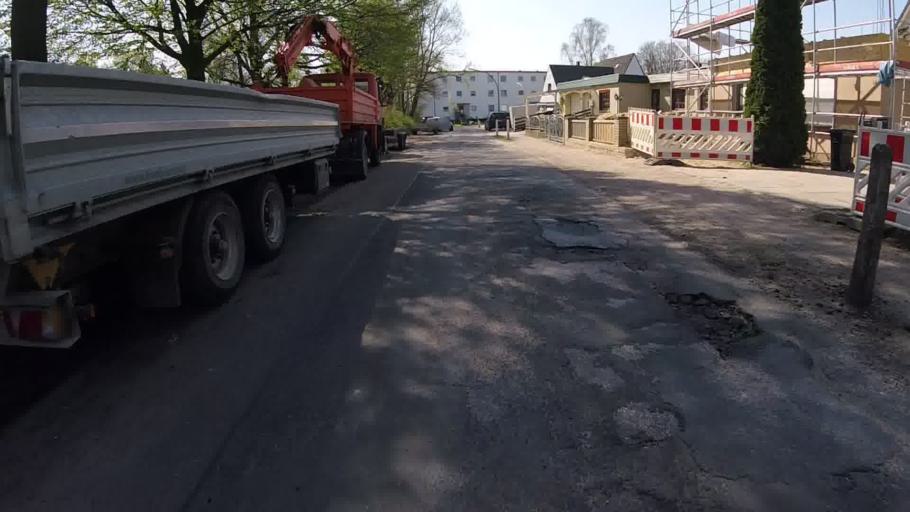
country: DE
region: Hamburg
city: Farmsen-Berne
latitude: 53.5898
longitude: 10.1418
